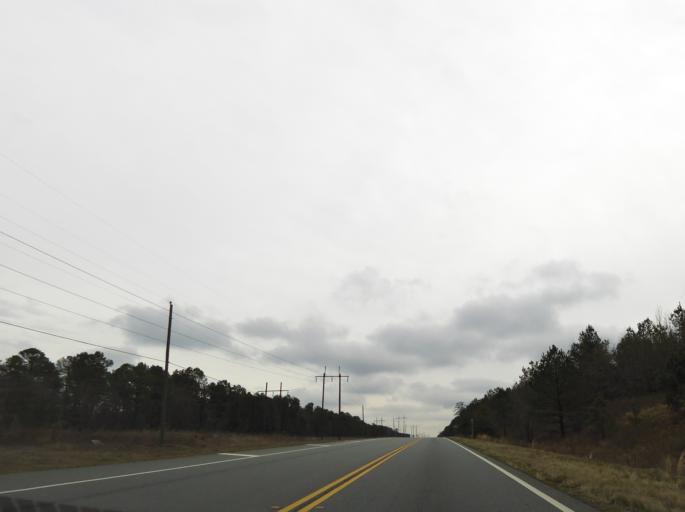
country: US
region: Georgia
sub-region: Houston County
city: Robins Air Force Base
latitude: 32.5416
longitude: -83.5034
